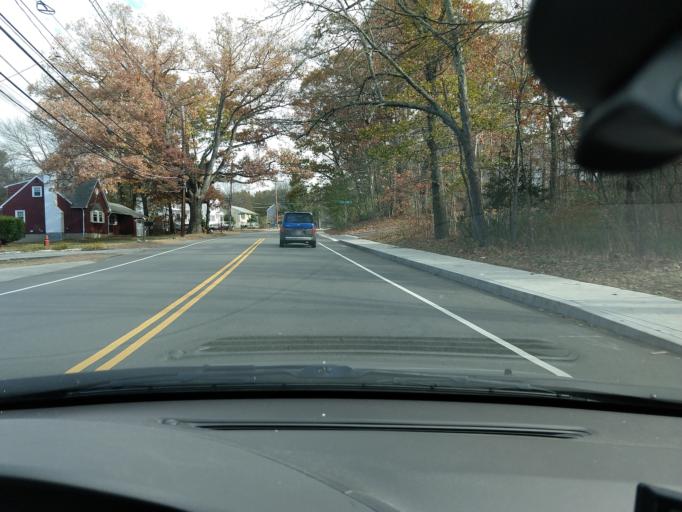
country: US
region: Massachusetts
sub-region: Middlesex County
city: Burlington
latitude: 42.5041
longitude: -71.2045
